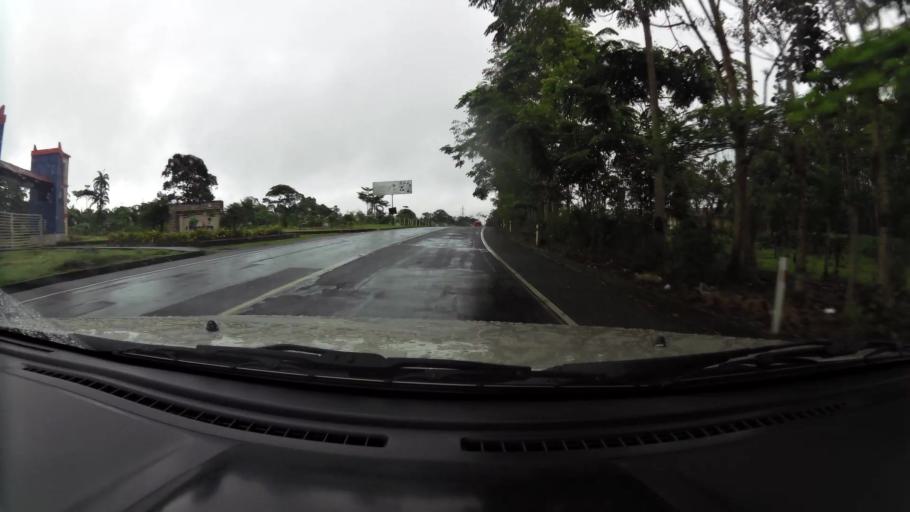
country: EC
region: Santo Domingo de los Tsachilas
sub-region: Canton Santo Domingo de los Colorados
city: Santo Domingo de los Colorados
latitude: -0.2350
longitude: -79.1327
